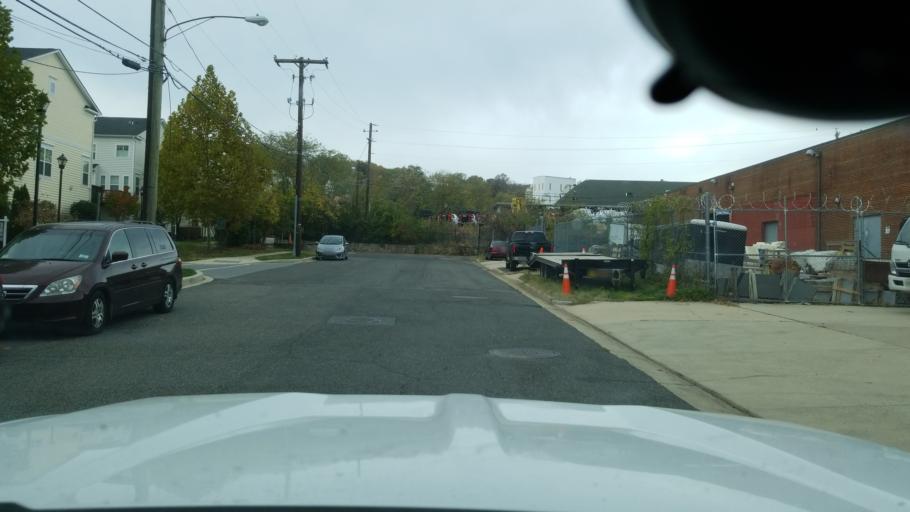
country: US
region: Maryland
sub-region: Prince George's County
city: Chillum
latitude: 38.9501
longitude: -76.9984
